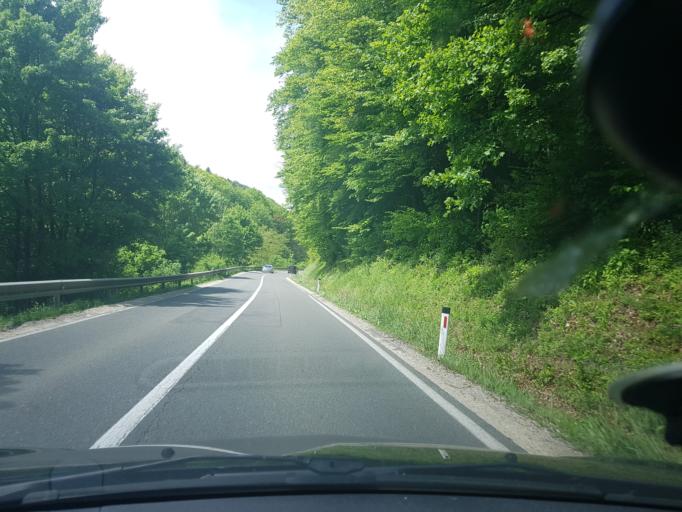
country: SI
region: Rogaska Slatina
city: Rogaska Slatina
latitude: 46.2406
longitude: 15.5895
